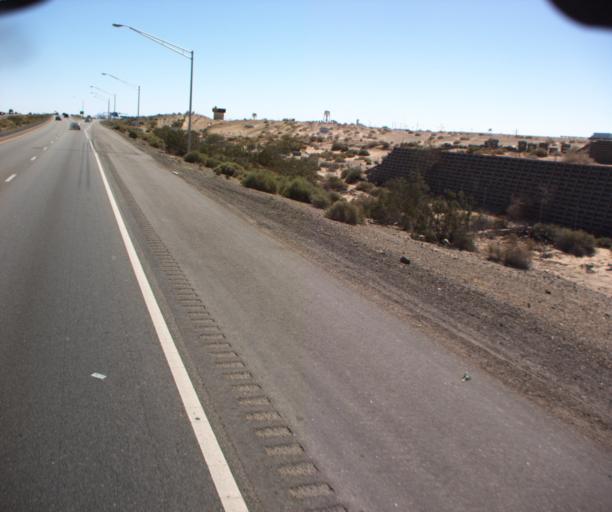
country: US
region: Arizona
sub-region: Yuma County
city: Yuma
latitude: 32.6902
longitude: -114.5888
